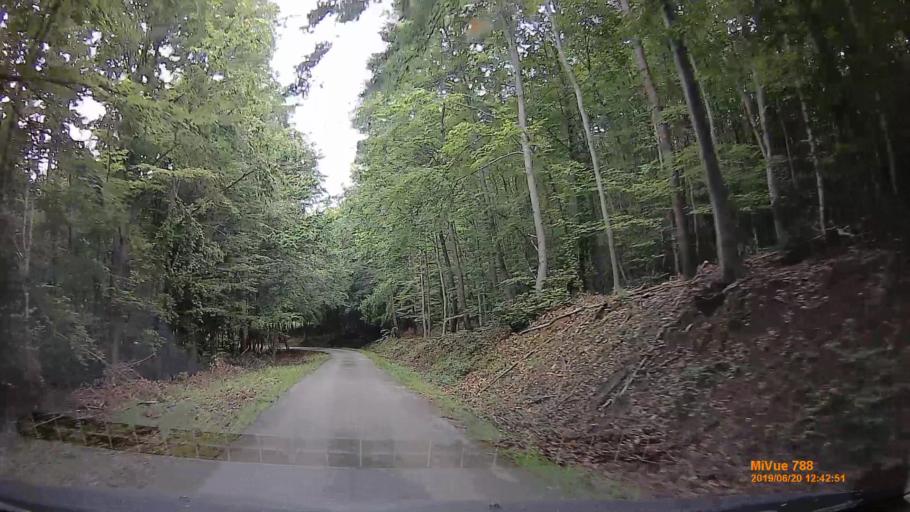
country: HU
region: Baranya
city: Hosszuheteny
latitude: 46.1992
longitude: 18.3585
